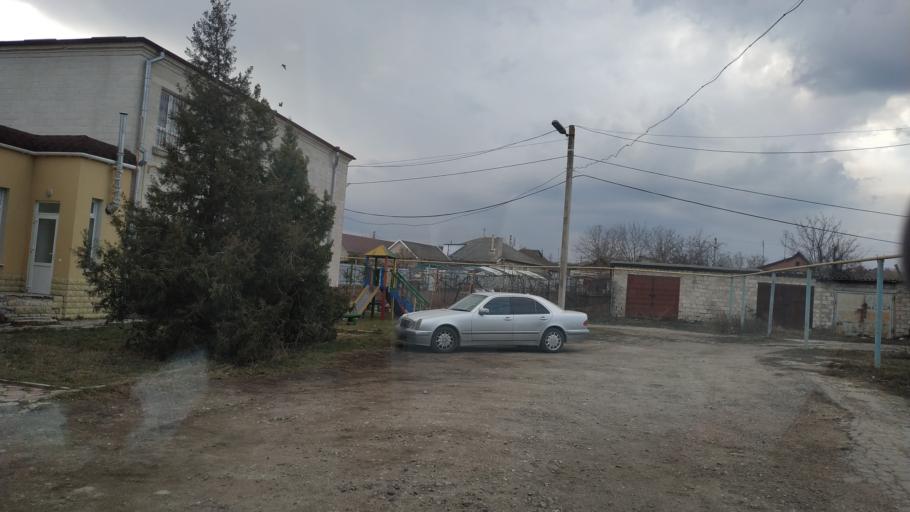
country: MD
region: Anenii Noi
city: Varnita
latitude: 46.8609
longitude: 29.4775
